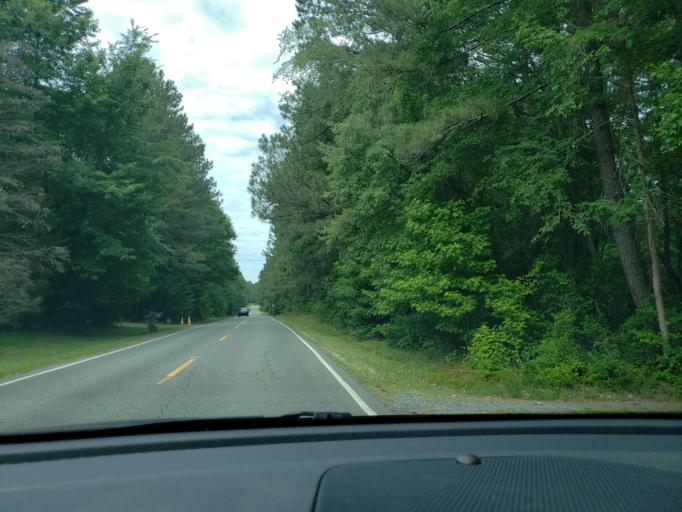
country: US
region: North Carolina
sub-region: Wake County
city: Green Level
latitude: 35.7923
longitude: -78.9890
